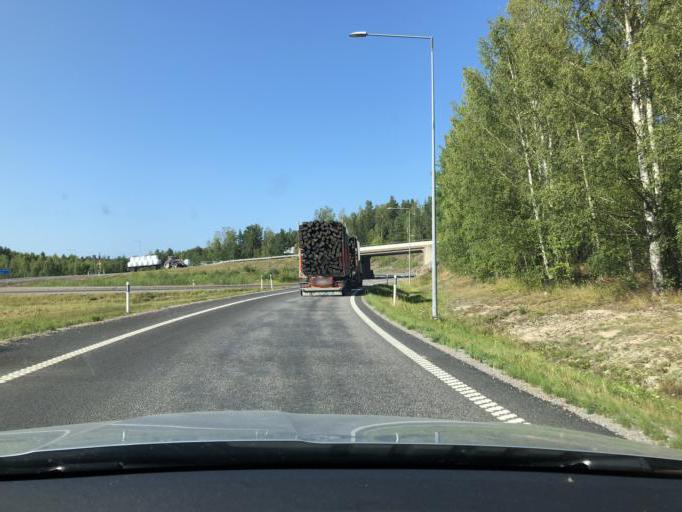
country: SE
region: Dalarna
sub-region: Faluns Kommun
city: Falun
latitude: 60.5851
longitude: 15.7709
